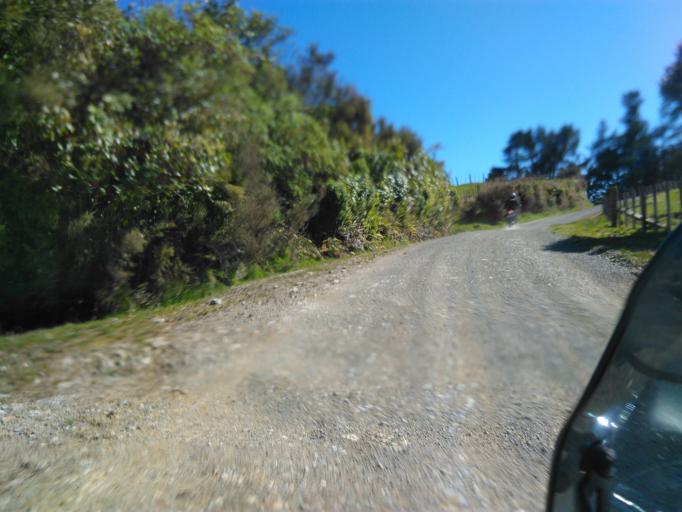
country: NZ
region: Bay of Plenty
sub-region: Opotiki District
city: Opotiki
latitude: -38.3559
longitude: 177.5897
